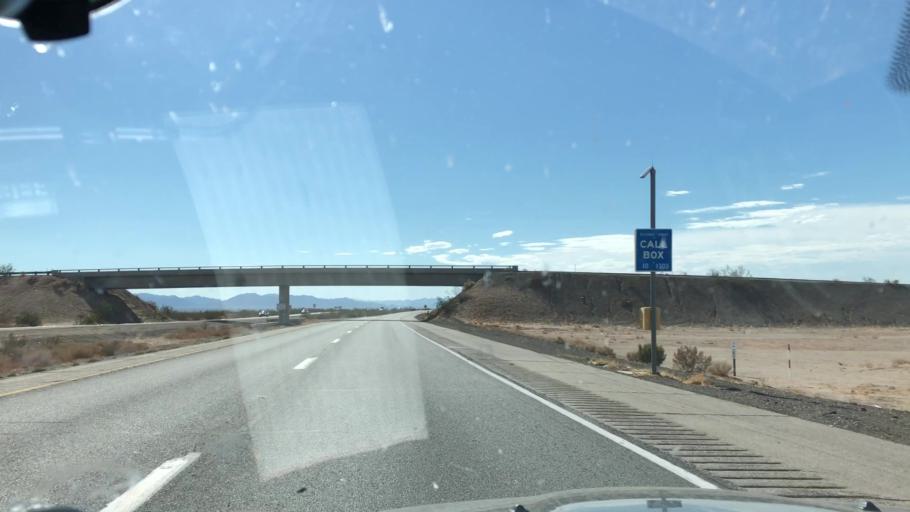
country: US
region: California
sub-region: Riverside County
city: Mesa Verde
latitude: 33.6074
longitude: -114.9886
